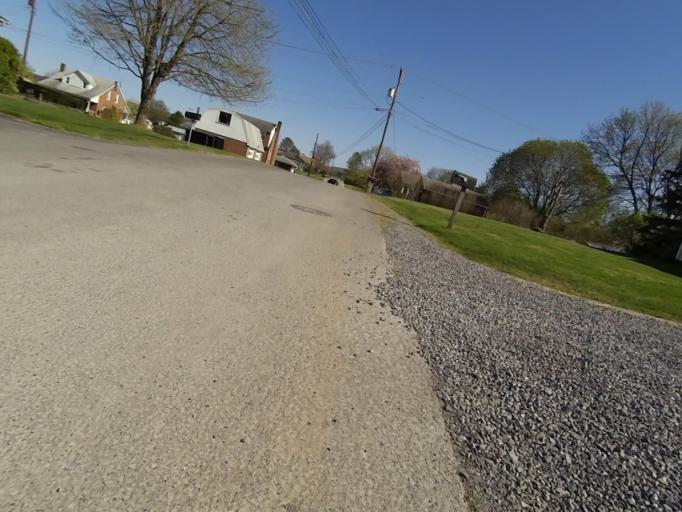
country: US
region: Pennsylvania
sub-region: Centre County
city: Bellefonte
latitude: 40.9115
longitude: -77.7890
